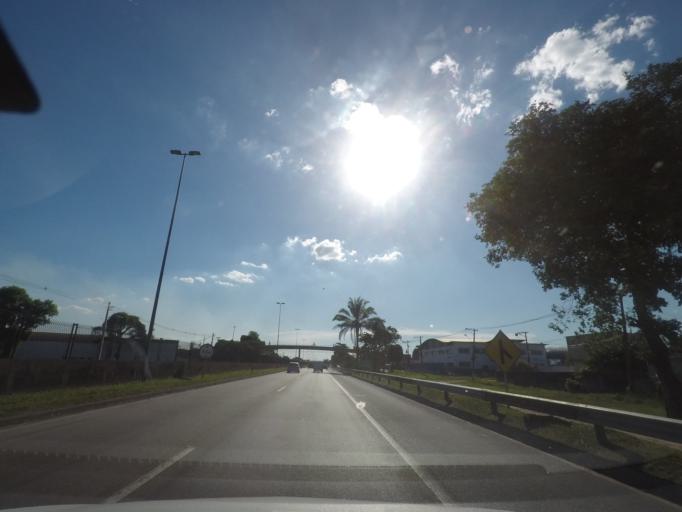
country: BR
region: Rio de Janeiro
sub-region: Petropolis
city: Petropolis
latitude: -22.6484
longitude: -43.2298
